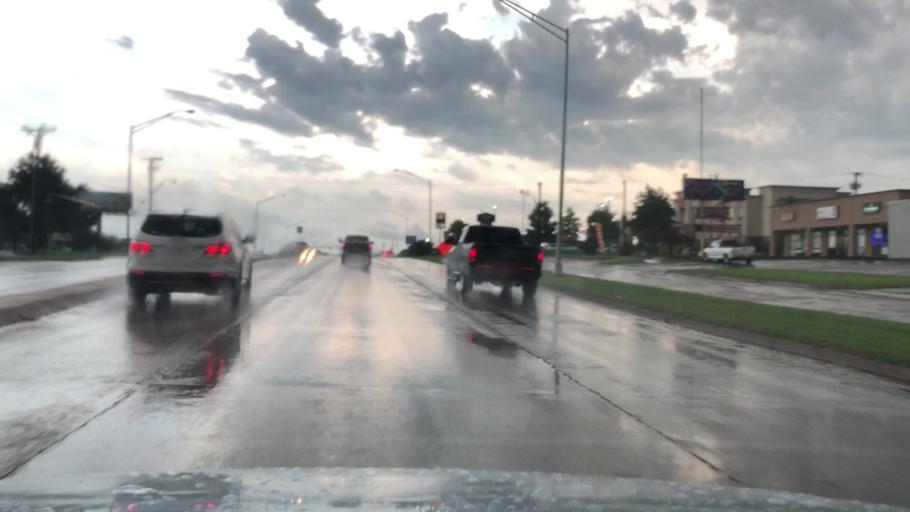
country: US
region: Oklahoma
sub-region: Washington County
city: Dewey
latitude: 36.7542
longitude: -95.9355
